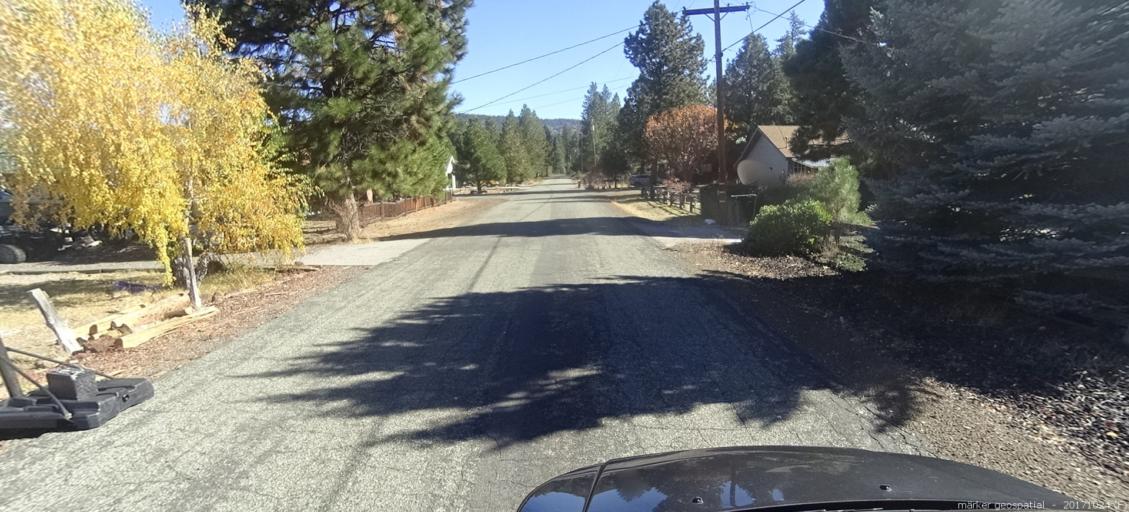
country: US
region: California
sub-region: Shasta County
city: Burney
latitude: 40.6717
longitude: -121.4313
